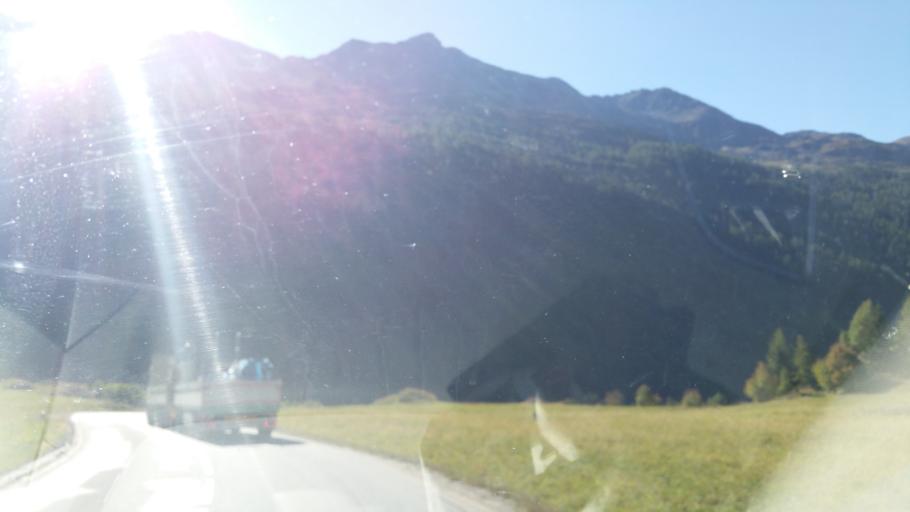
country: IT
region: Piedmont
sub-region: Provincia di Torino
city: Moncenisio
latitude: 45.2969
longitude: 6.9333
